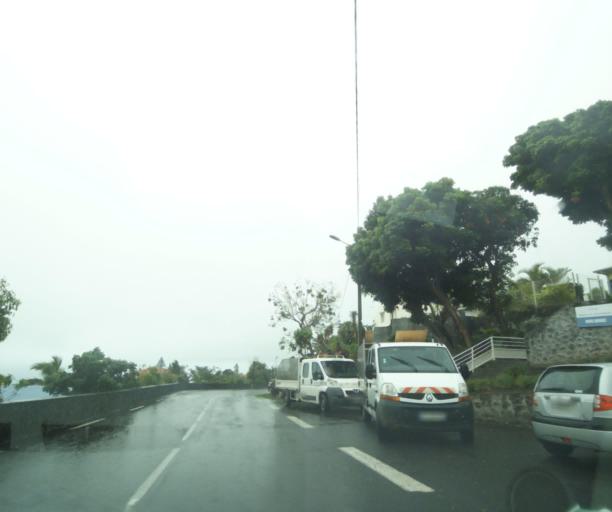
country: RE
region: Reunion
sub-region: Reunion
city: Saint-Paul
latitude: -21.0298
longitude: 55.2851
